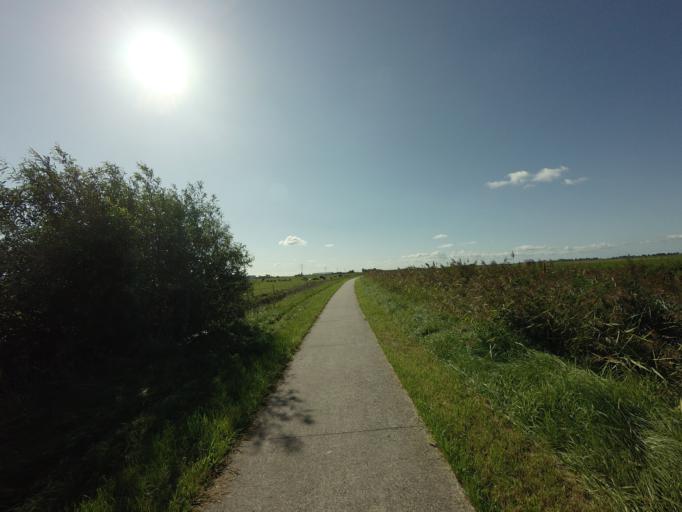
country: NL
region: Friesland
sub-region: Gemeente Boarnsterhim
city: Reduzum
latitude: 53.1446
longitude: 5.7644
